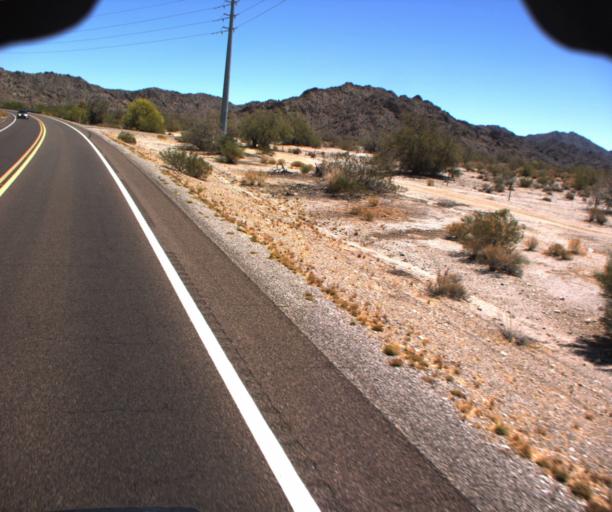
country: US
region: Arizona
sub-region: La Paz County
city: Salome
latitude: 33.7249
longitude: -113.6879
